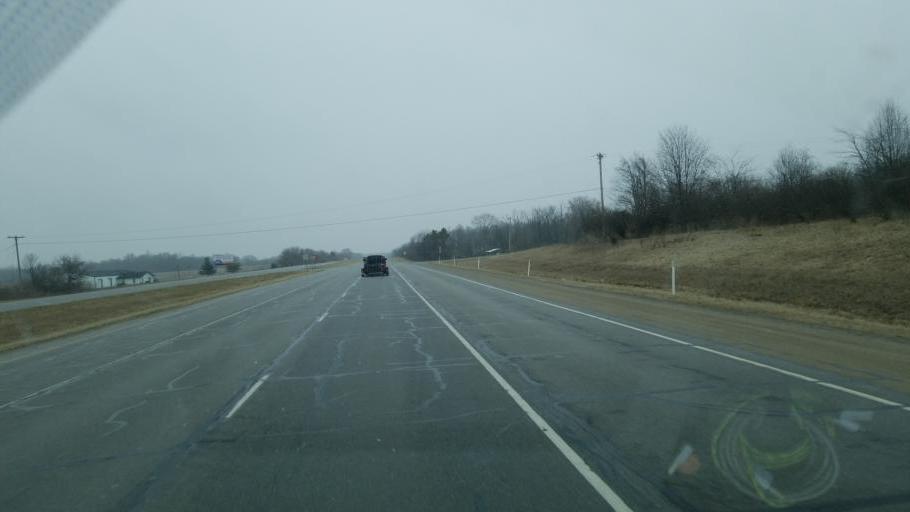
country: US
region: Indiana
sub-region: Miami County
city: Peru
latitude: 40.7922
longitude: -86.0408
